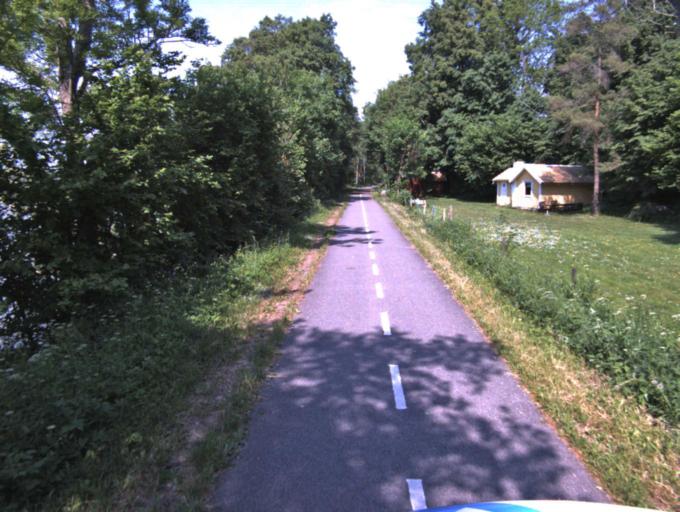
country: SE
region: Skane
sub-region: Kristianstads Kommun
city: Fjalkinge
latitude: 56.0903
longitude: 14.2333
